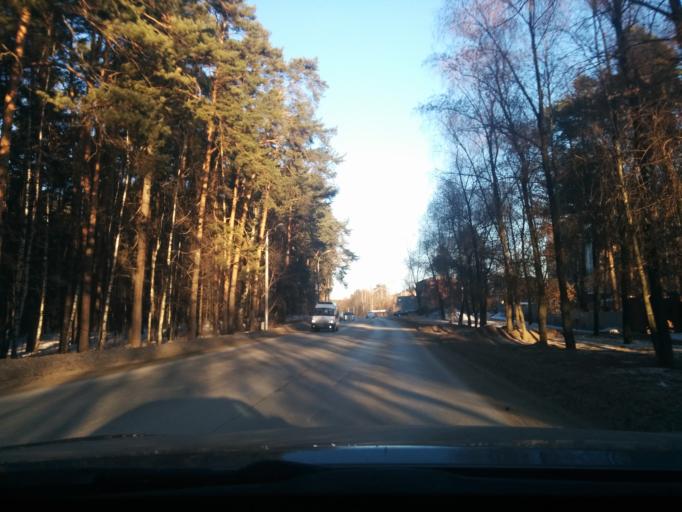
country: RU
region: Perm
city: Kultayevo
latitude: 58.0090
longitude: 55.9766
